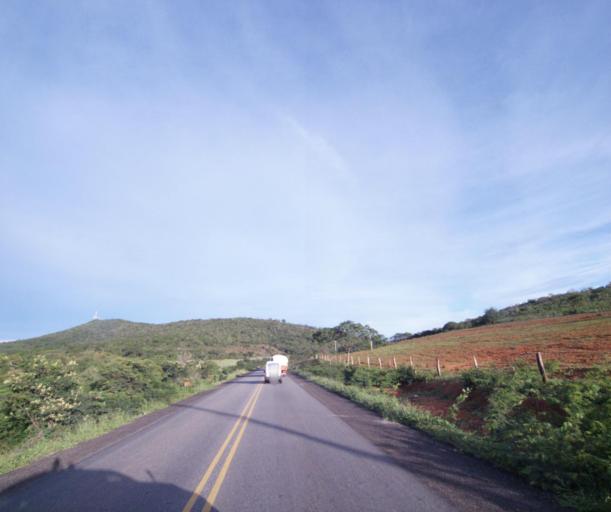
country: BR
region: Bahia
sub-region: Cacule
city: Cacule
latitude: -14.1931
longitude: -42.1459
